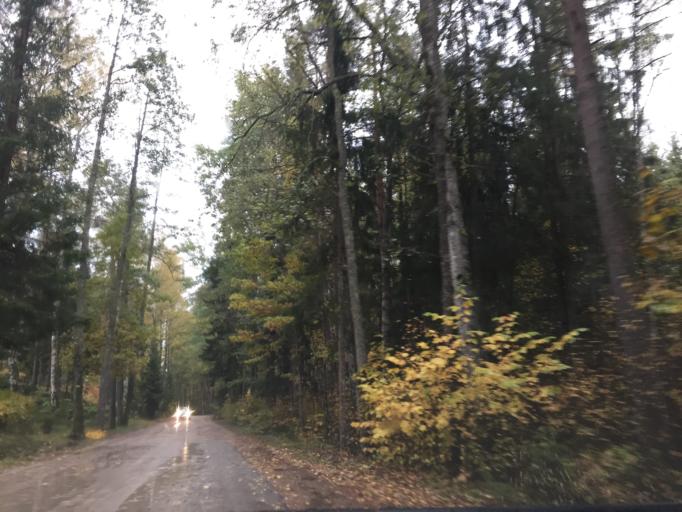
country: LV
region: Engure
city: Smarde
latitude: 56.9302
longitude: 23.4772
